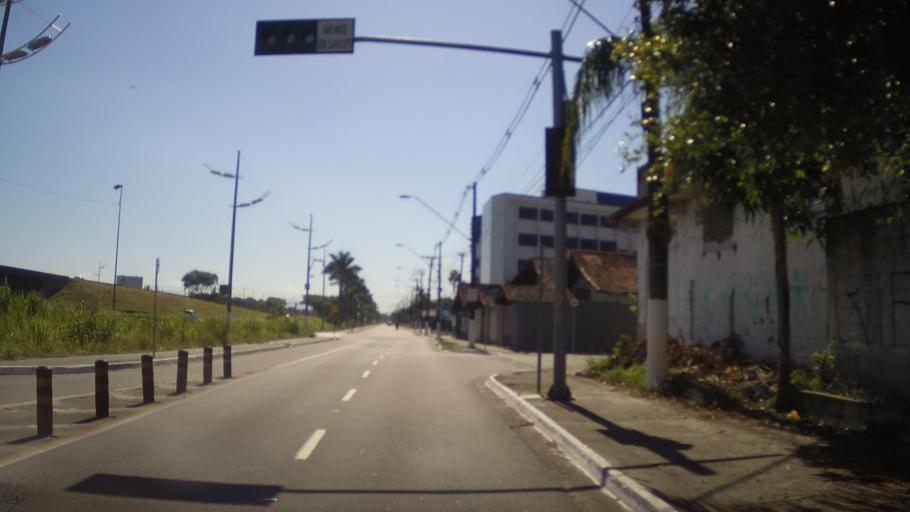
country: BR
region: Sao Paulo
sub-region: Praia Grande
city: Praia Grande
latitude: -24.0328
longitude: -46.5082
